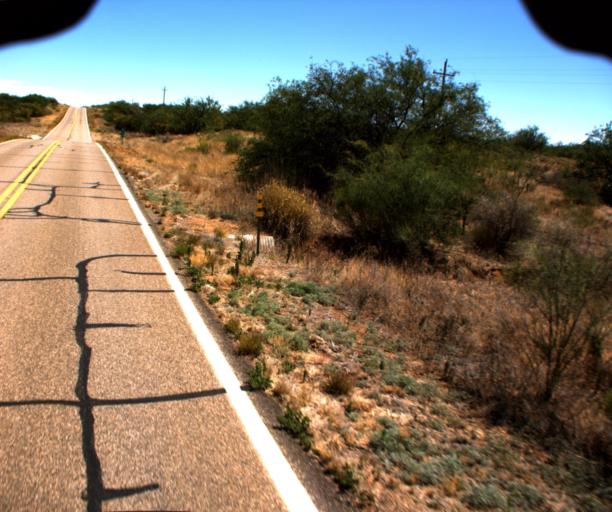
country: US
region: Arizona
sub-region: Pima County
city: Three Points
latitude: 31.7156
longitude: -111.4878
